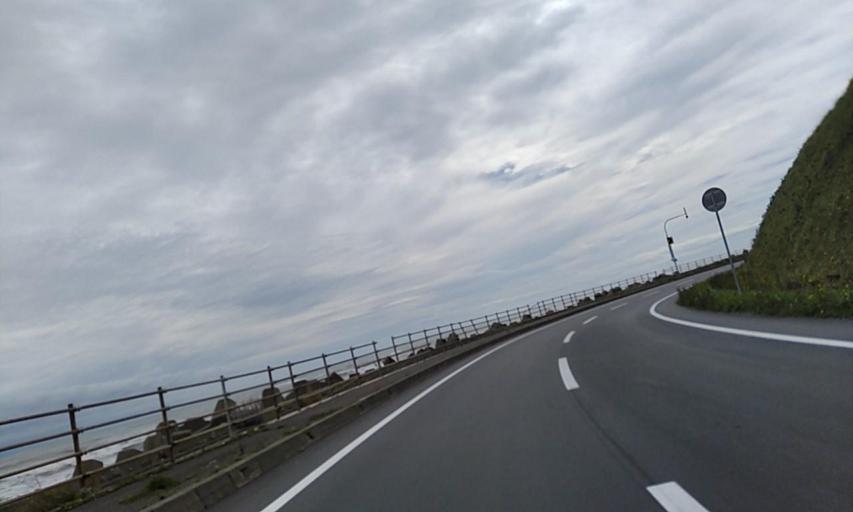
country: JP
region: Hokkaido
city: Kushiro
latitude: 42.7926
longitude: 143.8035
